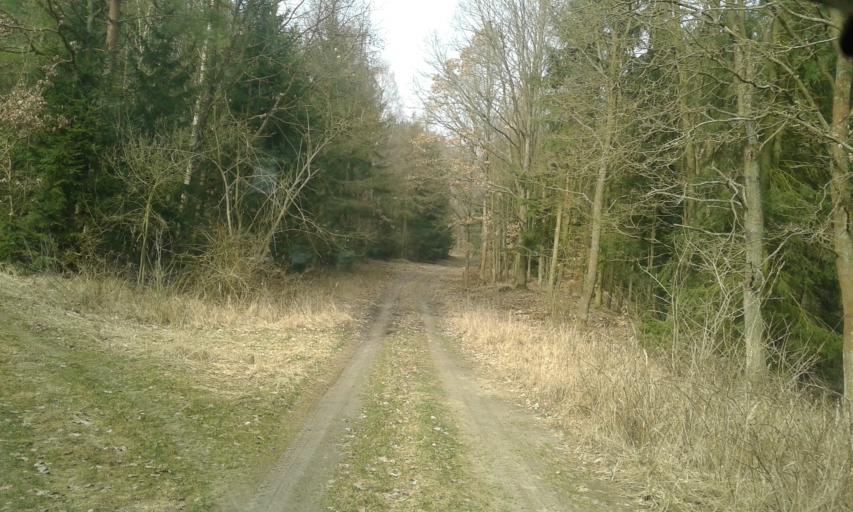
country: PL
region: West Pomeranian Voivodeship
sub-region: Powiat choszczenski
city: Pelczyce
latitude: 53.0886
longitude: 15.2327
